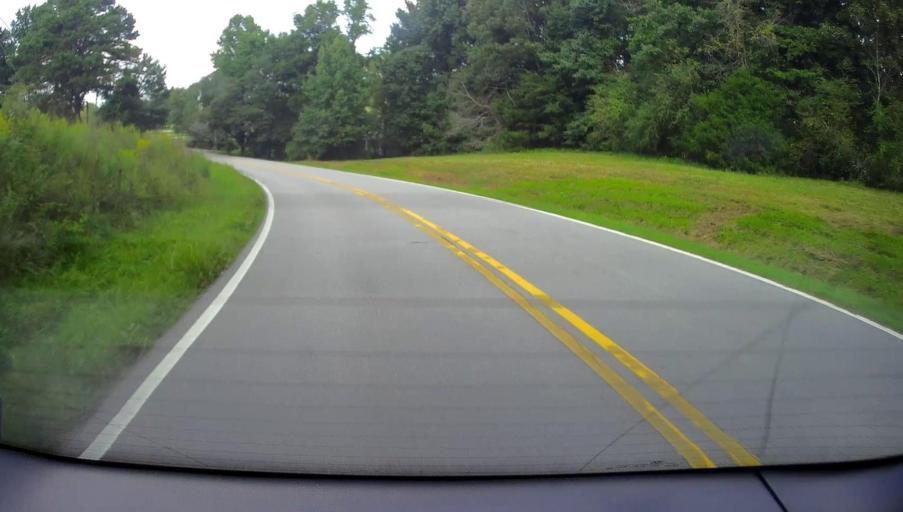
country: US
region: Georgia
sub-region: Catoosa County
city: Ringgold
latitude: 34.9220
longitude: -85.0849
